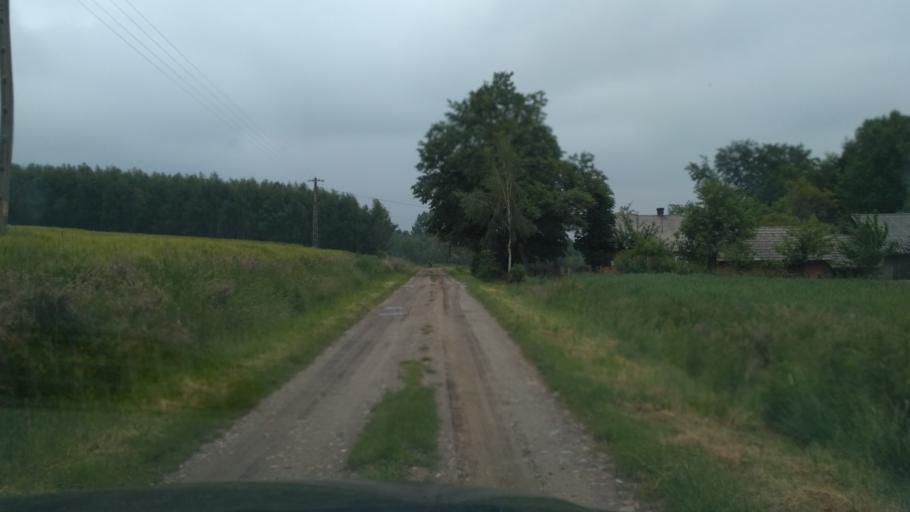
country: PL
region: Subcarpathian Voivodeship
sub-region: Powiat ropczycko-sedziszowski
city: Zagorzyce
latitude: 49.9809
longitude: 21.7087
